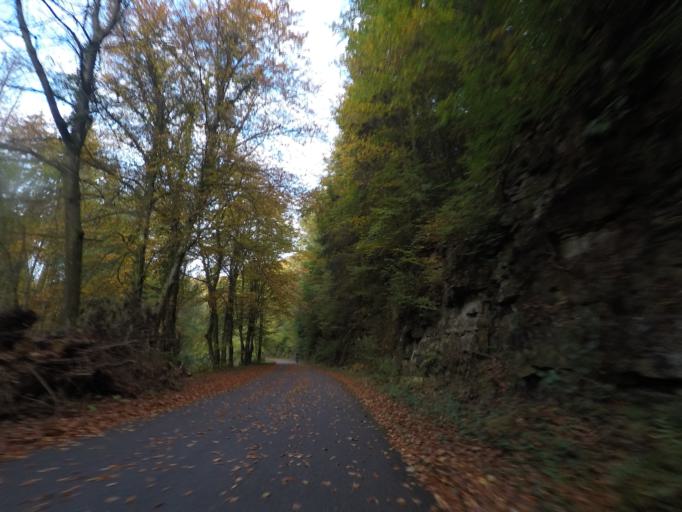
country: LU
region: Luxembourg
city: Itzig
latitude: 49.6016
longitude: 6.1682
